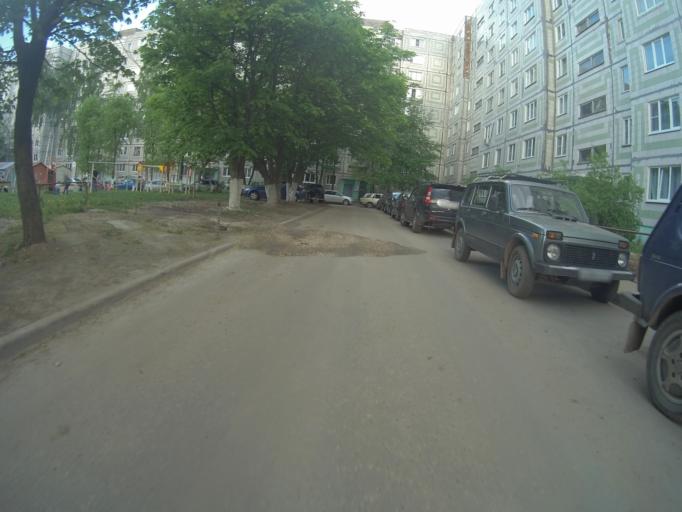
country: RU
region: Vladimir
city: Vladimir
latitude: 56.1703
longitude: 40.4432
